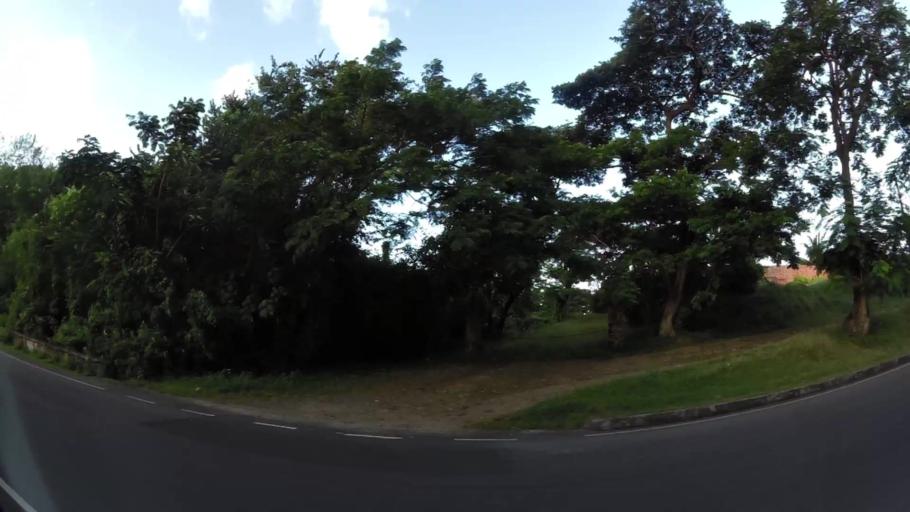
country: LC
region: Castries Quarter
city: Bisee
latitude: 14.0386
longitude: -60.9689
